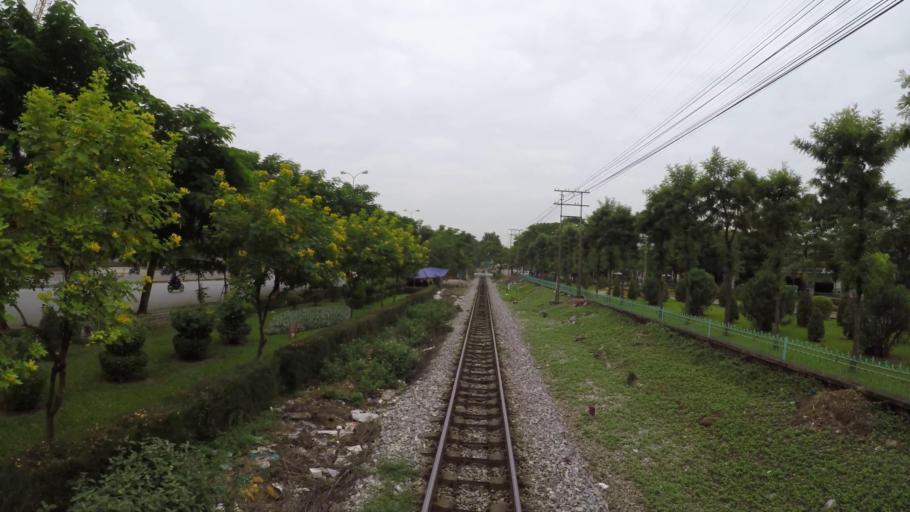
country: VN
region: Hai Phong
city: An Duong
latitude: 20.8766
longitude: 106.6335
